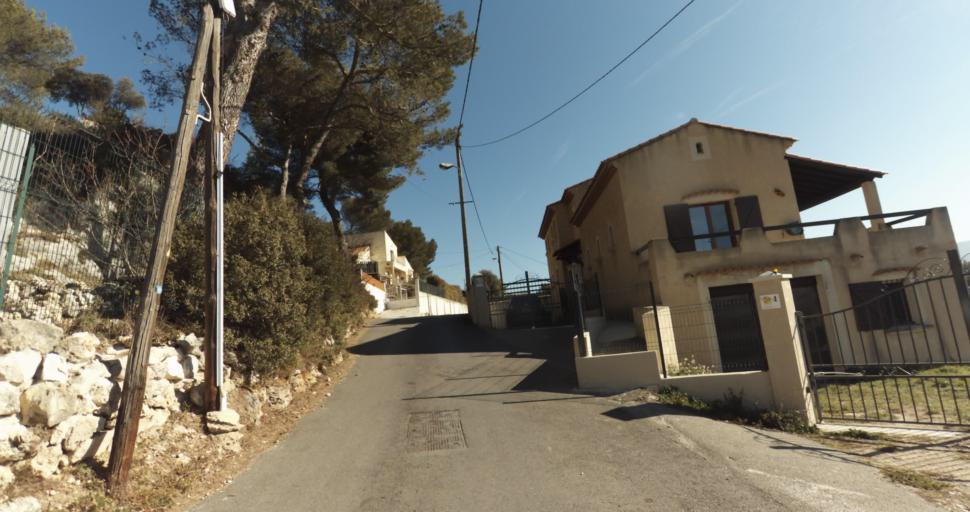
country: FR
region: Provence-Alpes-Cote d'Azur
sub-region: Departement des Bouches-du-Rhone
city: Peypin
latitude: 43.3870
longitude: 5.5800
